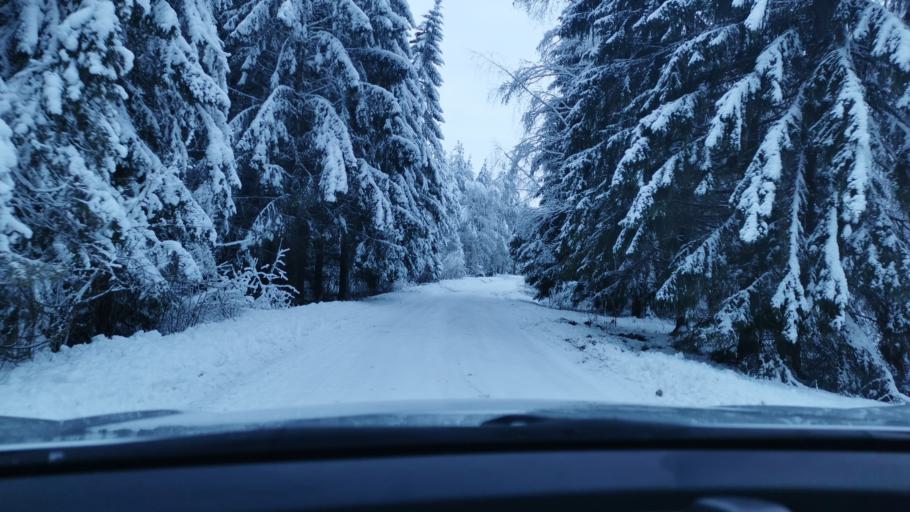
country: EE
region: Laeaene-Virumaa
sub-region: Someru vald
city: Someru
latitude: 59.4625
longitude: 26.4170
